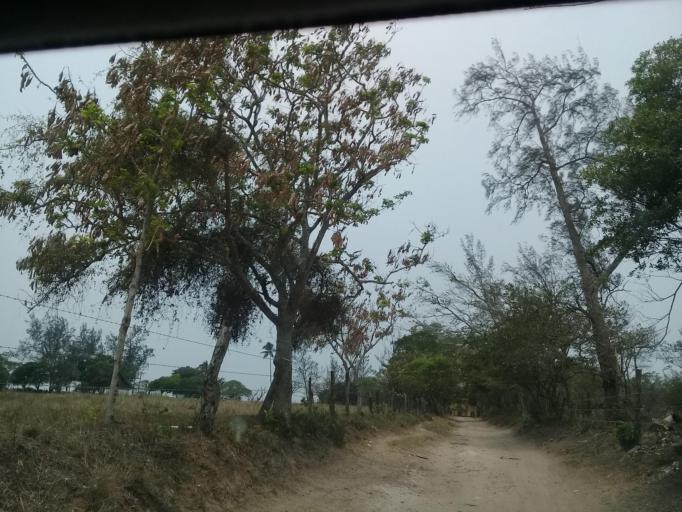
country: MX
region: Veracruz
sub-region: Veracruz
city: Las Amapolas
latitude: 19.1473
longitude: -96.2096
